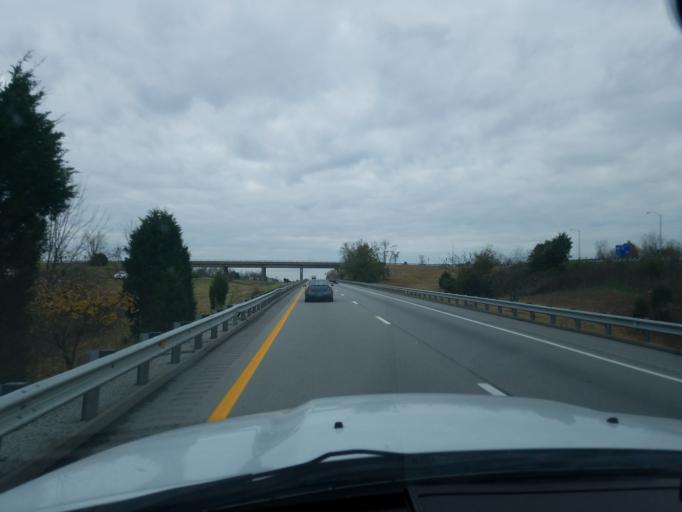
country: US
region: Kentucky
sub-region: Trimble County
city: Providence
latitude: 38.5217
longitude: -85.2338
